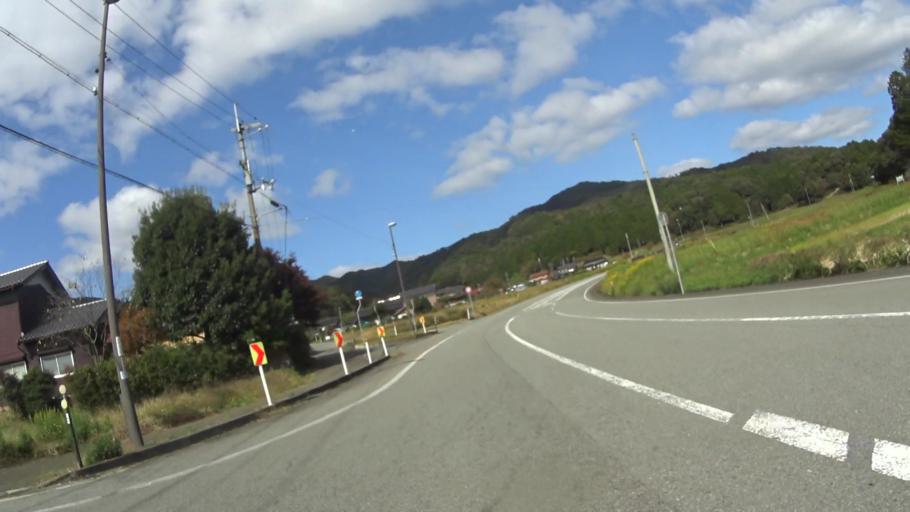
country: JP
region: Hyogo
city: Toyooka
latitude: 35.5061
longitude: 134.9908
